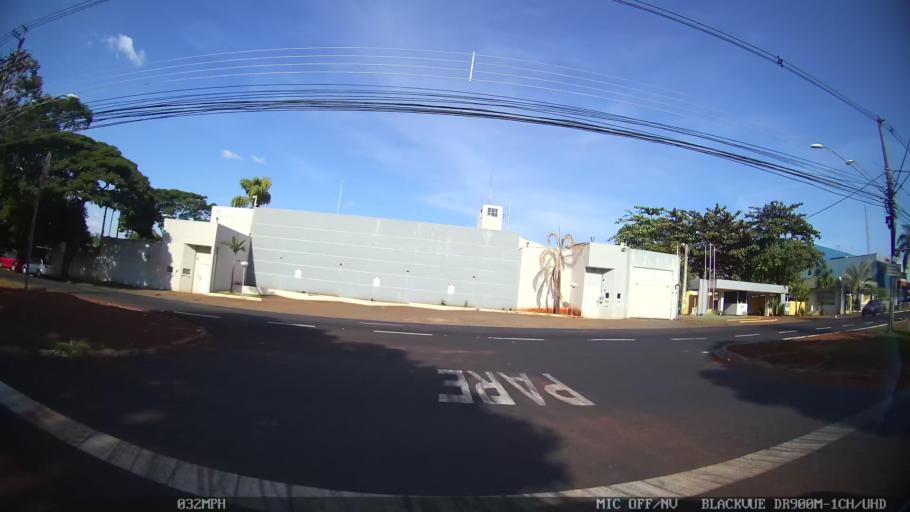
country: BR
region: Sao Paulo
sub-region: Ribeirao Preto
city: Ribeirao Preto
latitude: -21.1965
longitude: -47.7637
